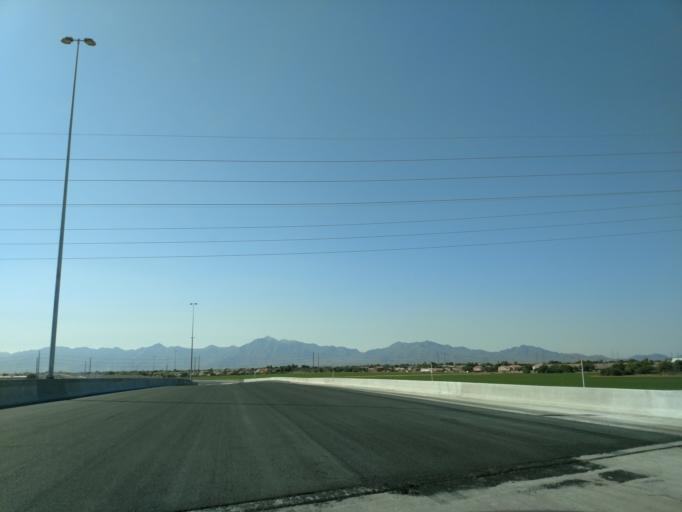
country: US
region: Arizona
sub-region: Maricopa County
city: Laveen
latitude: 33.4224
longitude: -112.1900
